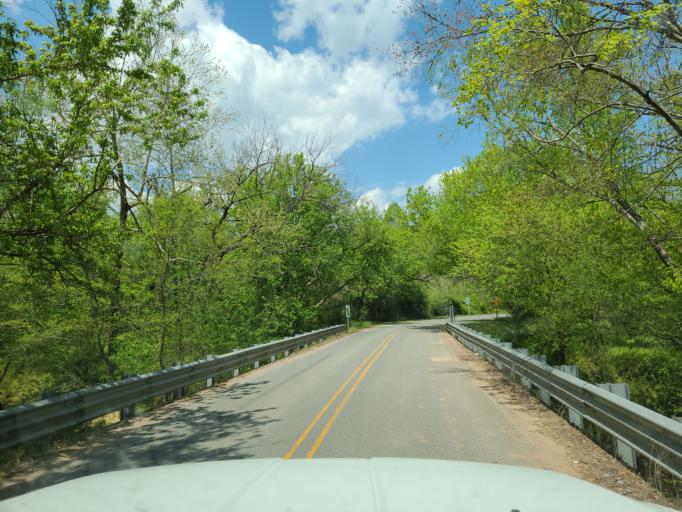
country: US
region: North Carolina
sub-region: Cleveland County
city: Shelby
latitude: 35.3265
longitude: -81.4765
